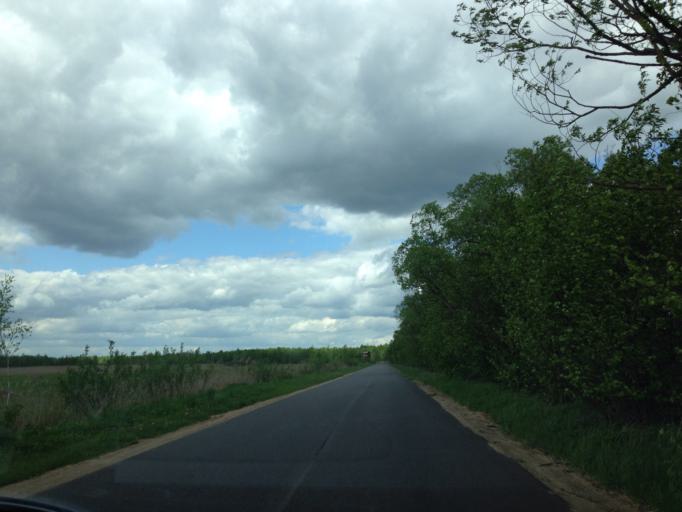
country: PL
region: Podlasie
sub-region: Powiat bialostocki
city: Tykocin
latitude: 53.2951
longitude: 22.6067
